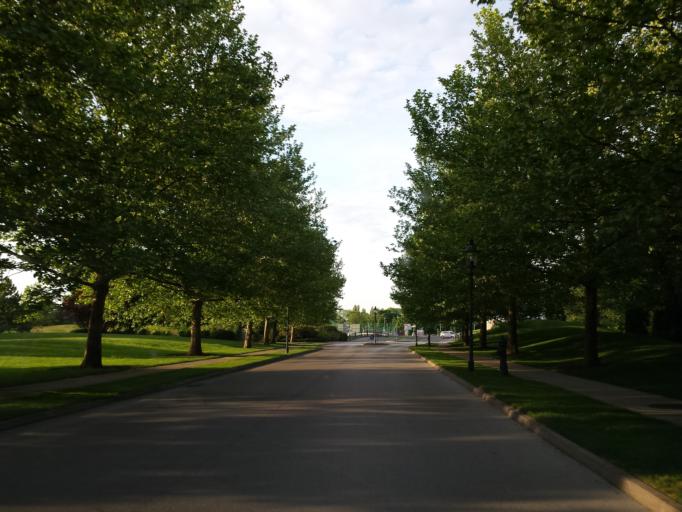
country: AT
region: Lower Austria
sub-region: Politischer Bezirk Baden
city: Oberwaltersdorf
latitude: 47.9789
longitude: 16.3169
